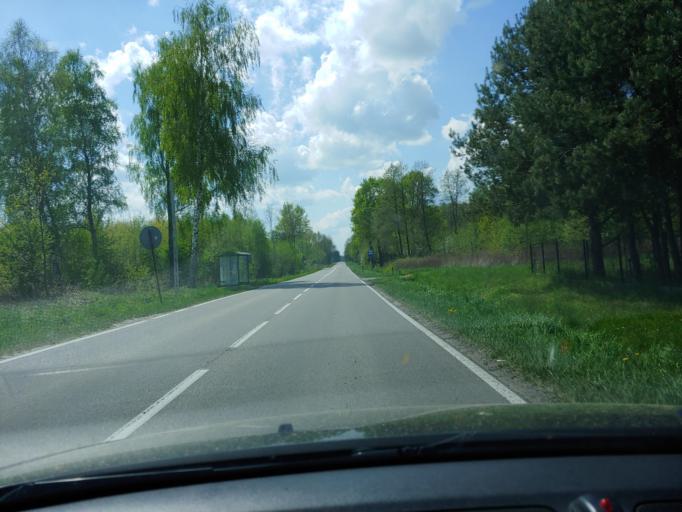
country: PL
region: Subcarpathian Voivodeship
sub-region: Powiat mielecki
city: Wadowice Gorne
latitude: 50.2529
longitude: 21.3204
